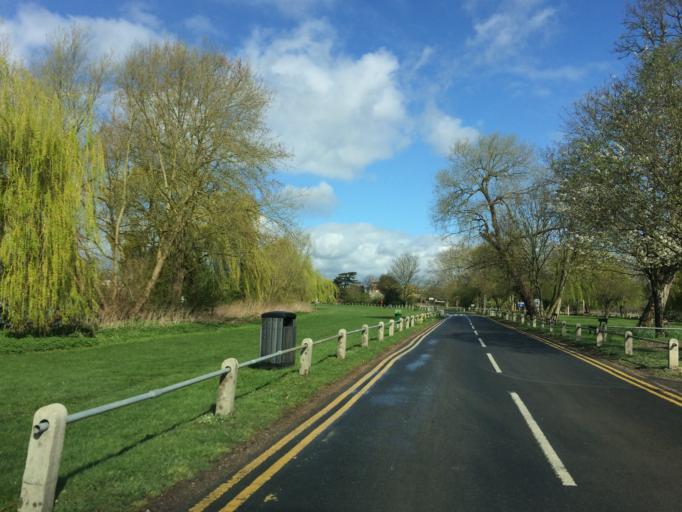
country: GB
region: England
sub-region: Surrey
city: Chertsey
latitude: 51.4039
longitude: -0.4907
